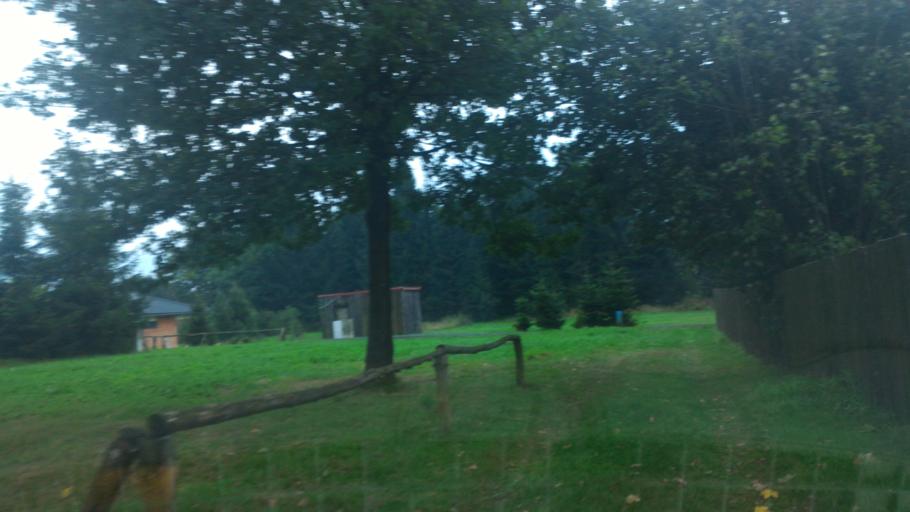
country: CZ
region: Ustecky
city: Dolni Podluzi
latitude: 50.9038
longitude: 14.5617
